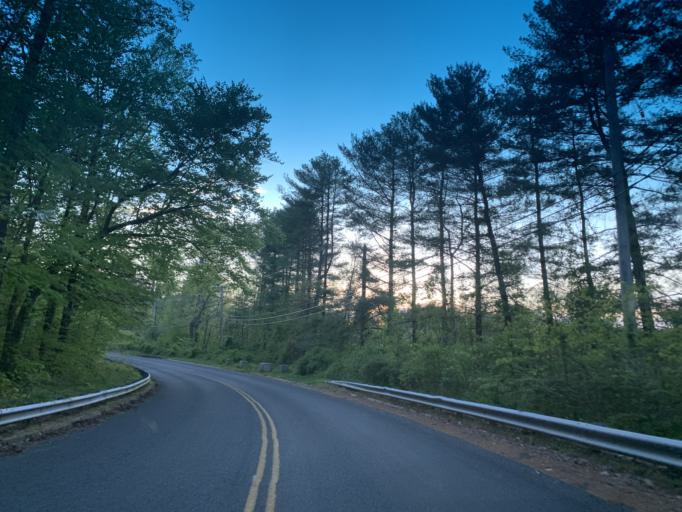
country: US
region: Maryland
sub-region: Harford County
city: Riverside
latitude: 39.5252
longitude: -76.2565
